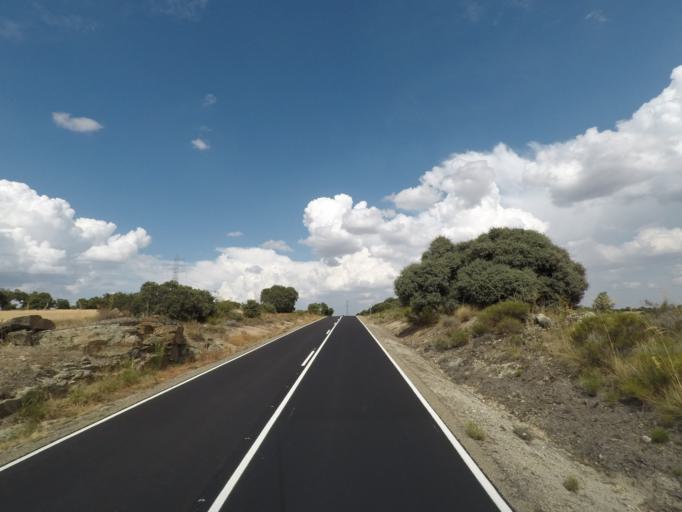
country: ES
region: Castille and Leon
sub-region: Provincia de Zamora
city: Fermoselle
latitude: 41.2981
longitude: -6.3288
